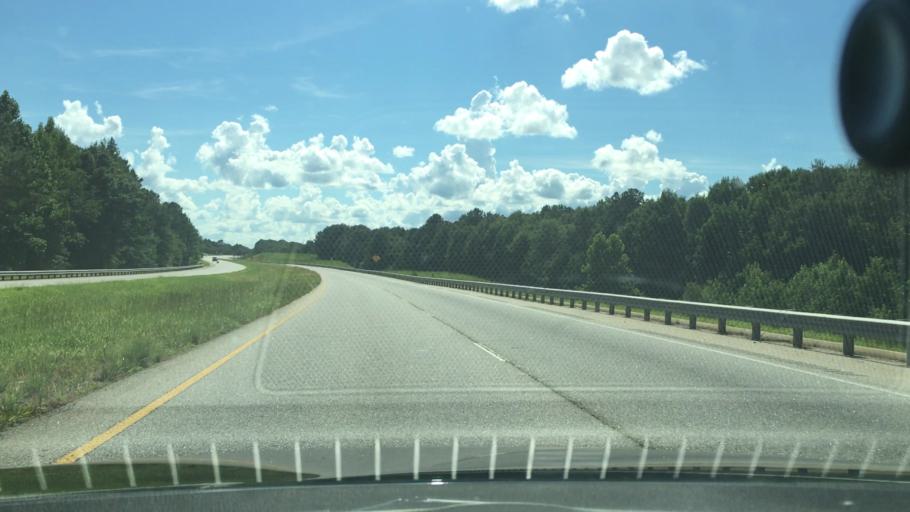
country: US
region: Georgia
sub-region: Spalding County
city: East Griffin
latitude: 33.2378
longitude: -84.2112
